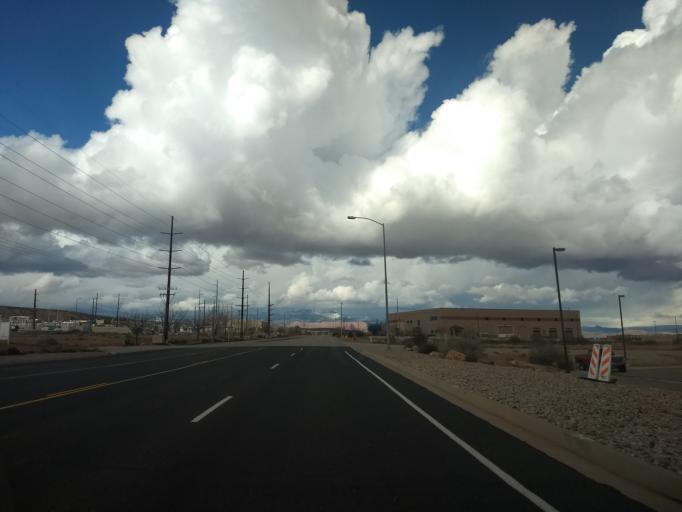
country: US
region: Utah
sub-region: Washington County
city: Saint George
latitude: 37.0283
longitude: -113.5630
